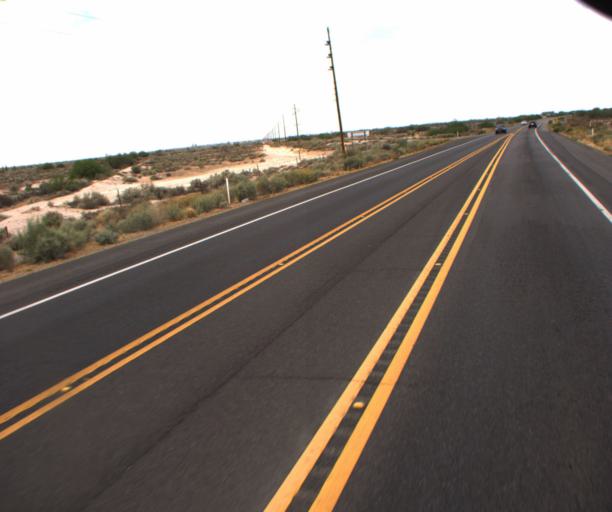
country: US
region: Arizona
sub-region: Pinal County
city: Sacaton
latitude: 33.0624
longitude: -111.6902
